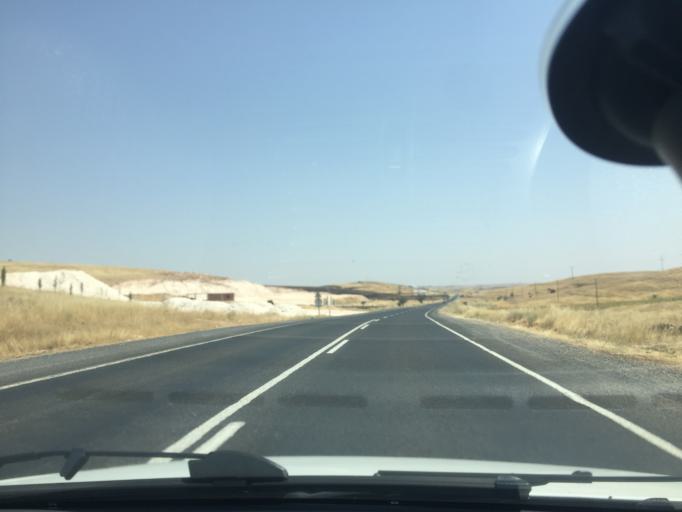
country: TR
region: Mardin
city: Kindirip
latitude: 37.4630
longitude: 41.2294
